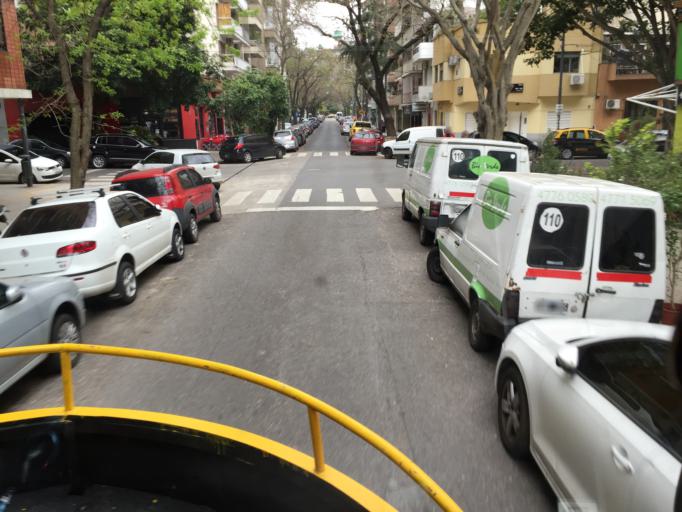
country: AR
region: Buenos Aires F.D.
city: Colegiales
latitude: -34.5705
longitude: -58.4343
